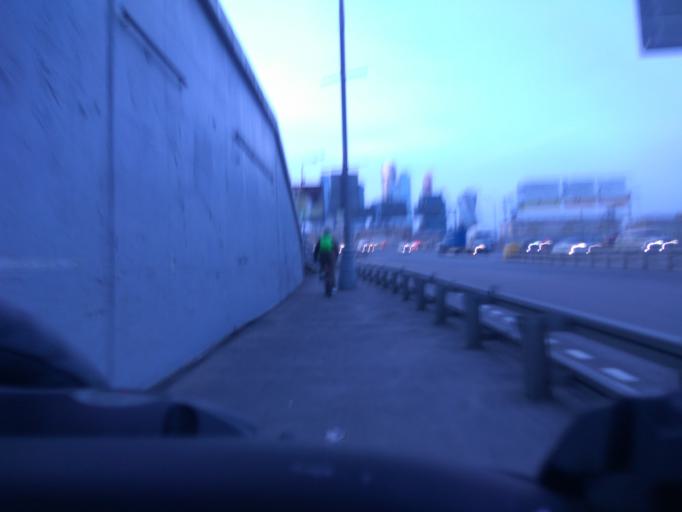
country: RU
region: Moskovskaya
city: Presnenskiy
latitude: 55.7334
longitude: 37.5428
